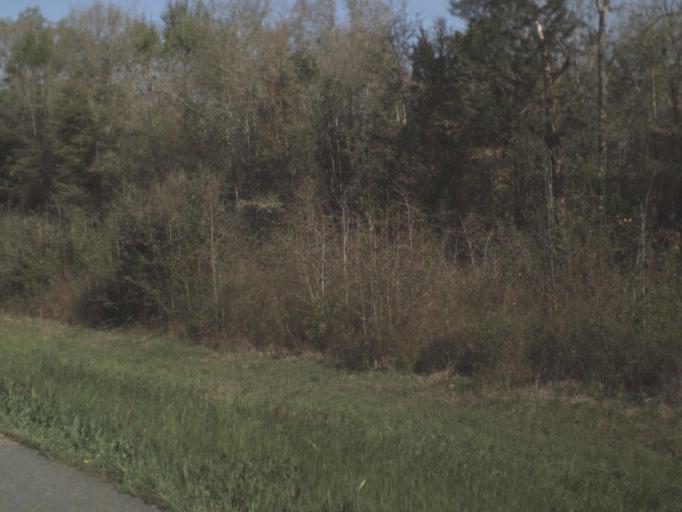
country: US
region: Alabama
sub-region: Houston County
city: Cottonwood
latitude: 30.9452
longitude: -85.3510
